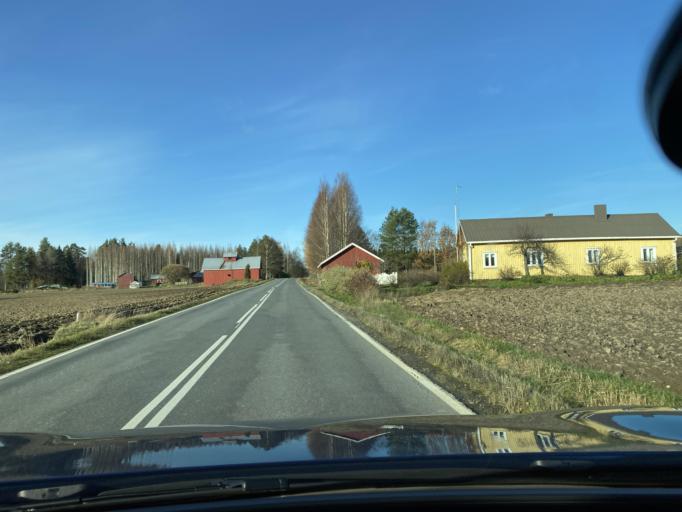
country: FI
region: Haeme
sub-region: Forssa
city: Tammela
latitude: 60.8359
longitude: 23.8379
